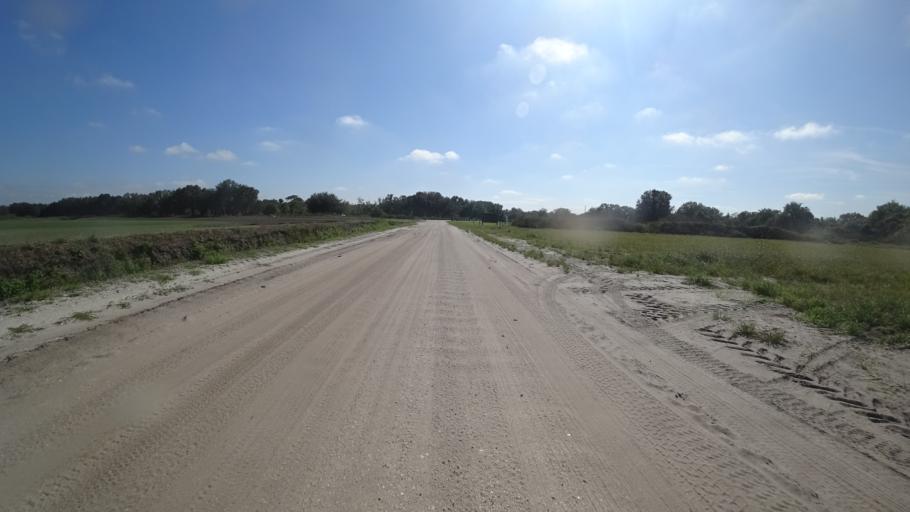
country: US
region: Florida
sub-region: DeSoto County
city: Arcadia
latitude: 27.2876
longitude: -82.0424
